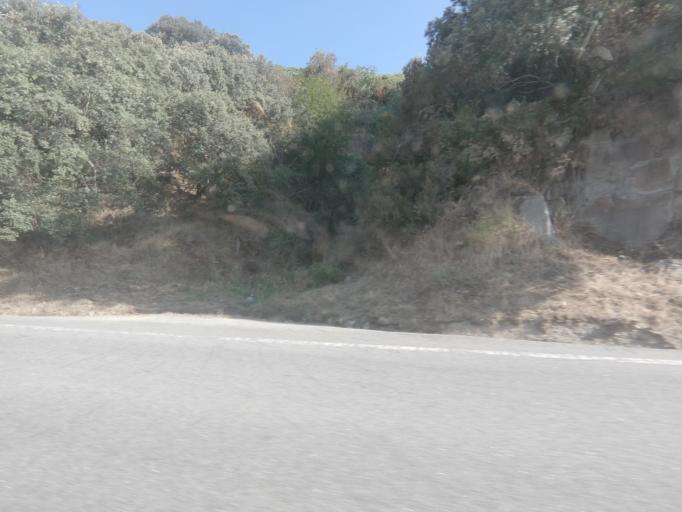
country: PT
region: Viseu
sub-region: Tabuaco
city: Tabuaco
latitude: 41.1547
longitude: -7.5926
